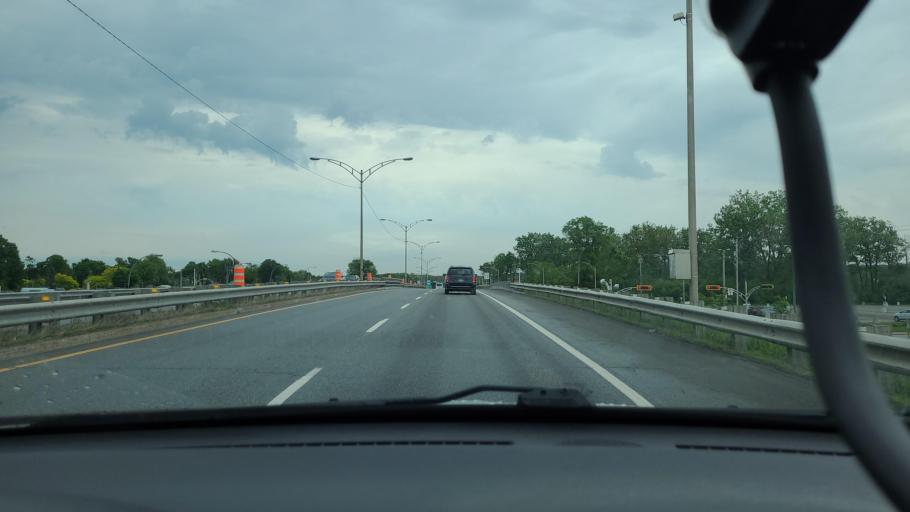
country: CA
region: Quebec
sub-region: Monteregie
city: Pincourt
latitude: 45.3863
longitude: -73.9945
